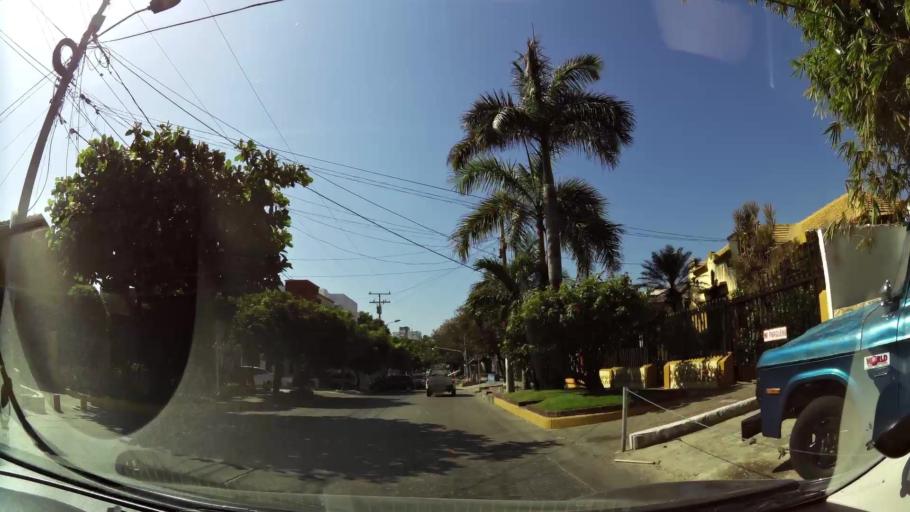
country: CO
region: Atlantico
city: Barranquilla
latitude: 10.9915
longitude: -74.8014
